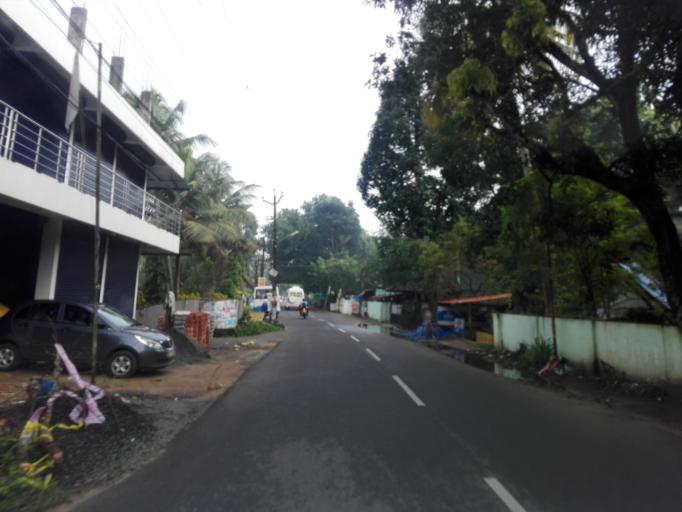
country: IN
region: Kerala
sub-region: Alappuzha
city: Arukutti
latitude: 9.9310
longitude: 76.3568
